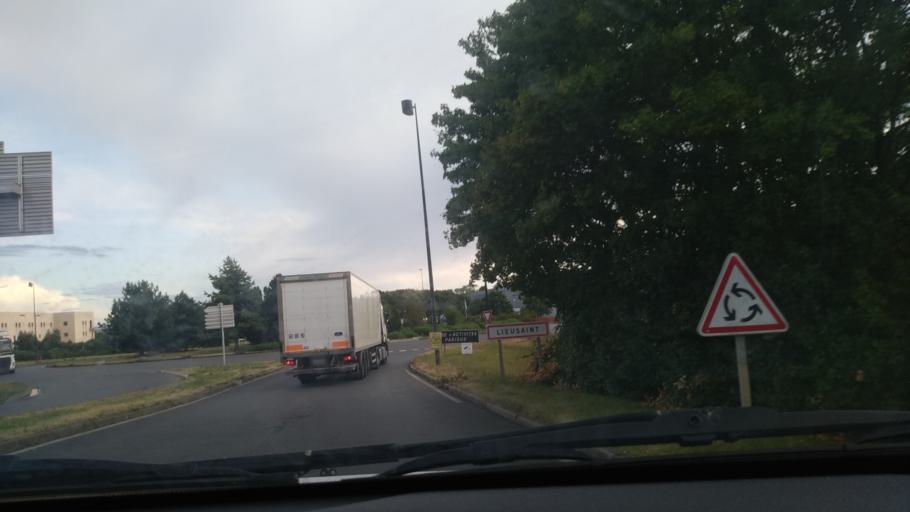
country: FR
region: Ile-de-France
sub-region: Departement de Seine-et-Marne
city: Lieusaint
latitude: 48.6437
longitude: 2.5496
